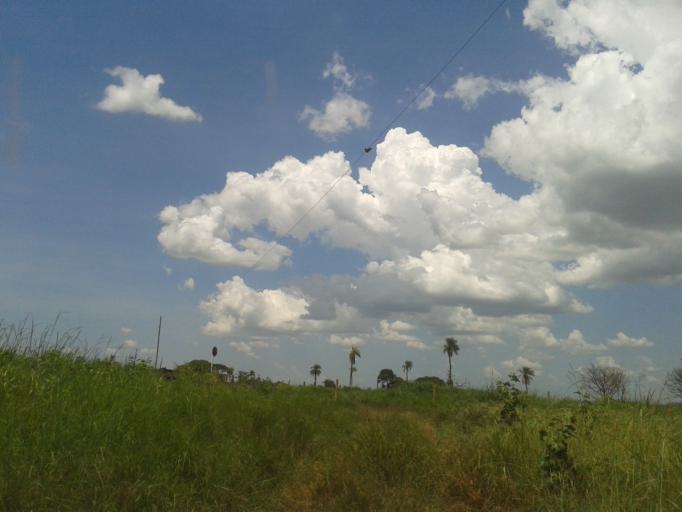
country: BR
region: Minas Gerais
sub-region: Santa Vitoria
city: Santa Vitoria
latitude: -19.1700
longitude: -50.4531
